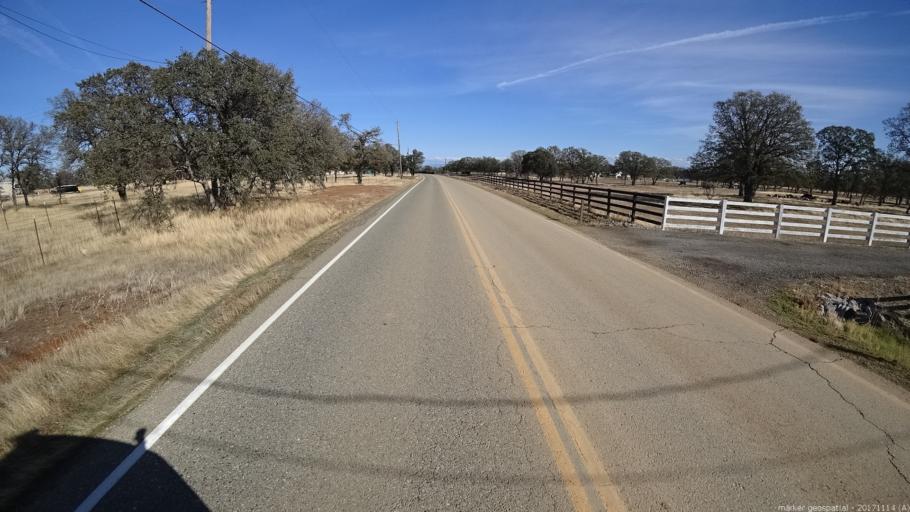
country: US
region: California
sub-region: Shasta County
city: Anderson
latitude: 40.4134
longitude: -122.3437
